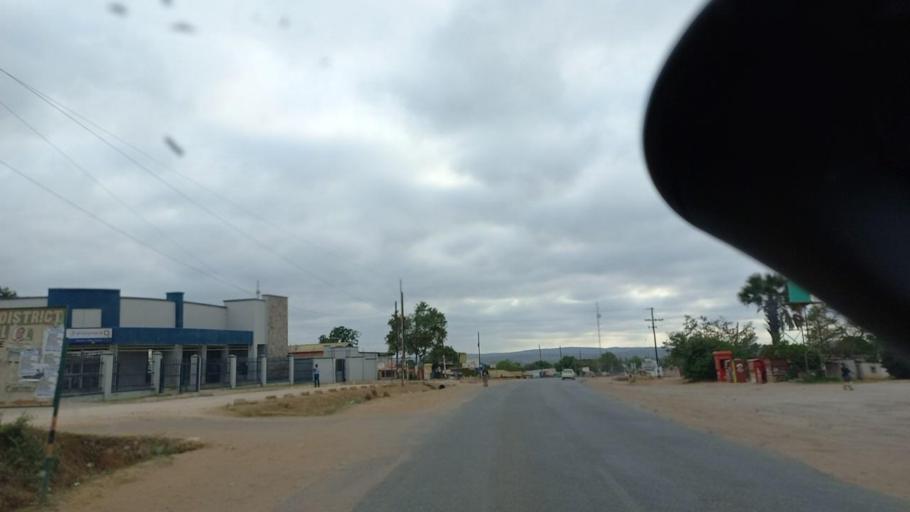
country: ZM
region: Lusaka
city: Chongwe
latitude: -15.3272
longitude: 28.6799
